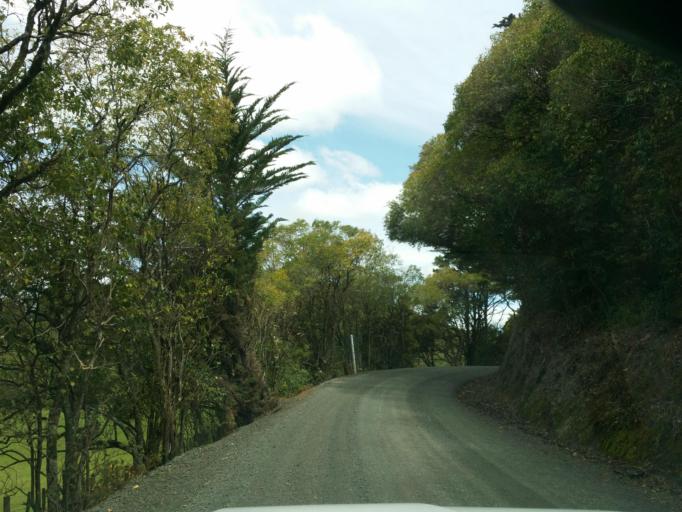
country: NZ
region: Northland
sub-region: Whangarei
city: Maungatapere
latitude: -35.8997
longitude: 174.1138
